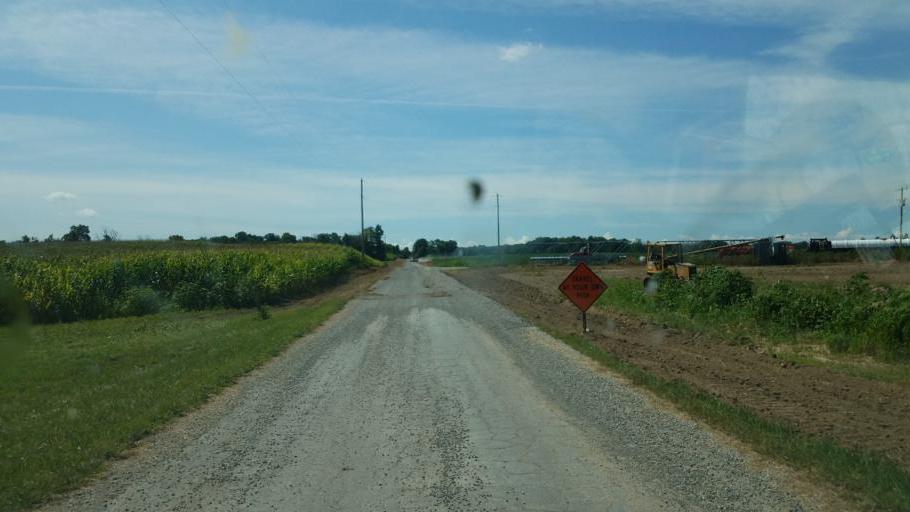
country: US
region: Ohio
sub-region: Knox County
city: Centerburg
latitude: 40.4477
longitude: -82.7170
